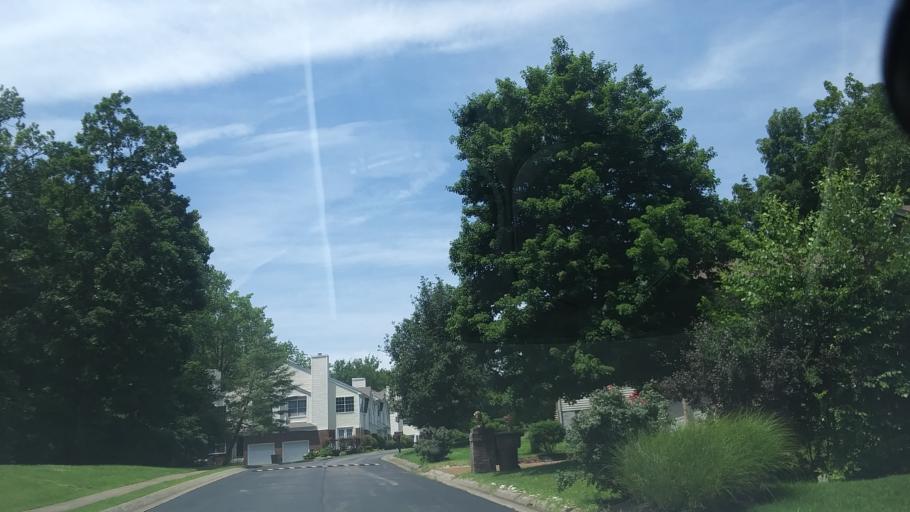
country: US
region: Tennessee
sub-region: Rutherford County
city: La Vergne
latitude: 36.0679
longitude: -86.6274
